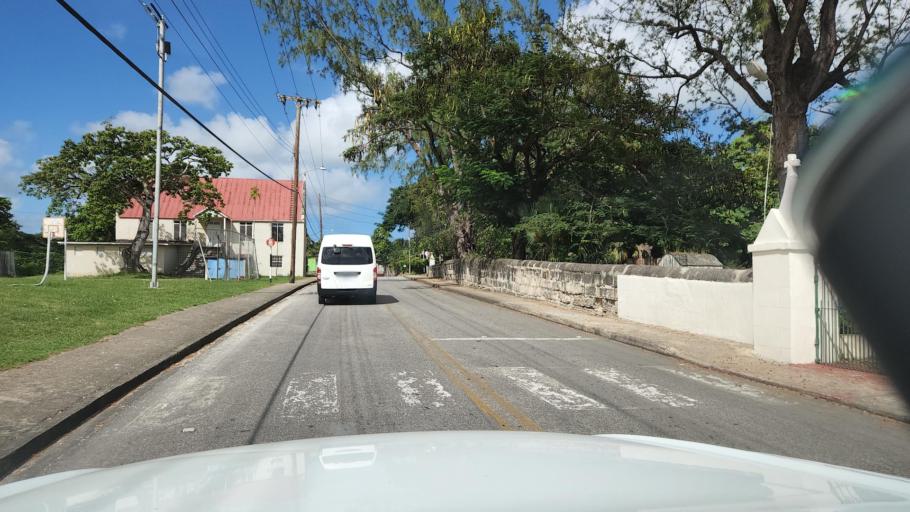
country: BB
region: Saint John
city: Four Cross Roads
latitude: 13.1368
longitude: -59.4890
